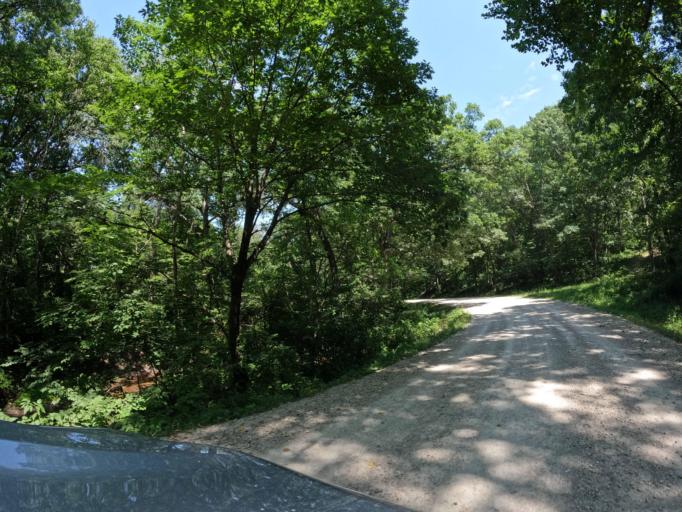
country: US
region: Iowa
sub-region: Henry County
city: Mount Pleasant
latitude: 40.8903
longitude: -91.6868
